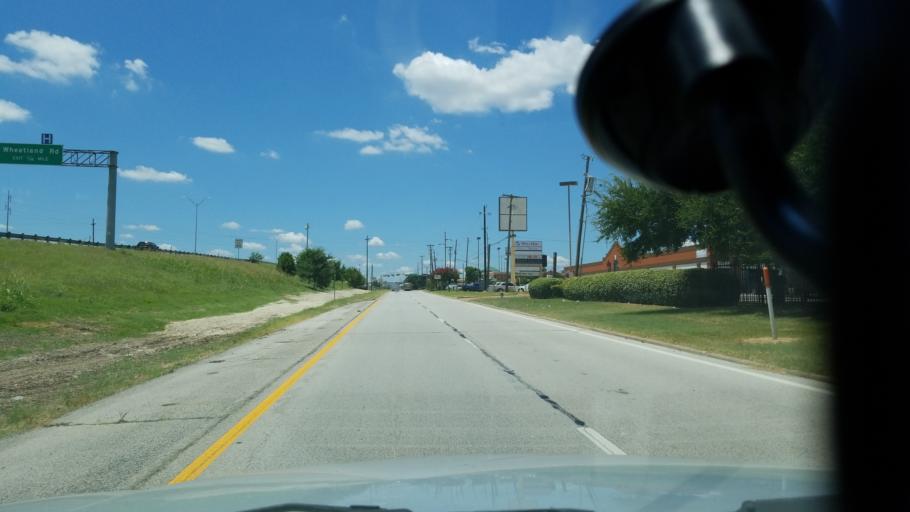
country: US
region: Texas
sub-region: Dallas County
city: Duncanville
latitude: 32.6640
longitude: -96.8689
